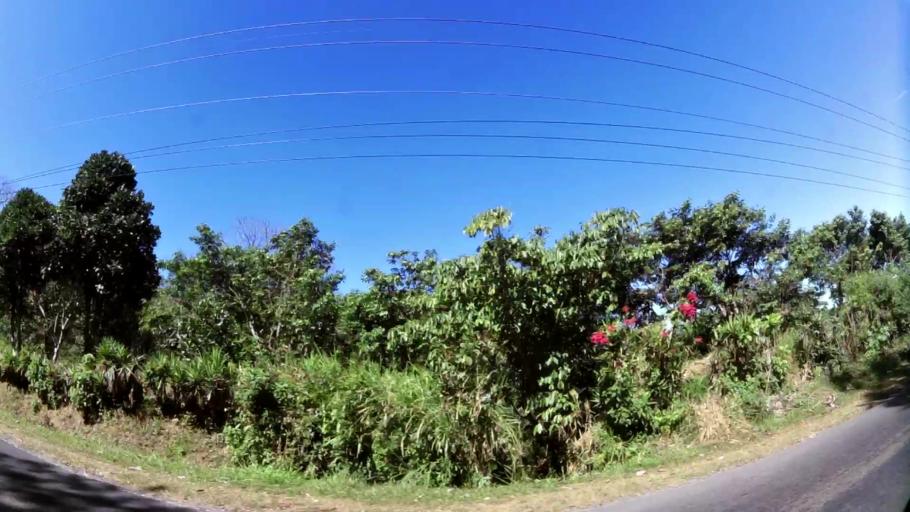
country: SV
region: Ahuachapan
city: Concepcion de Ataco
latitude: 13.8810
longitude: -89.8445
